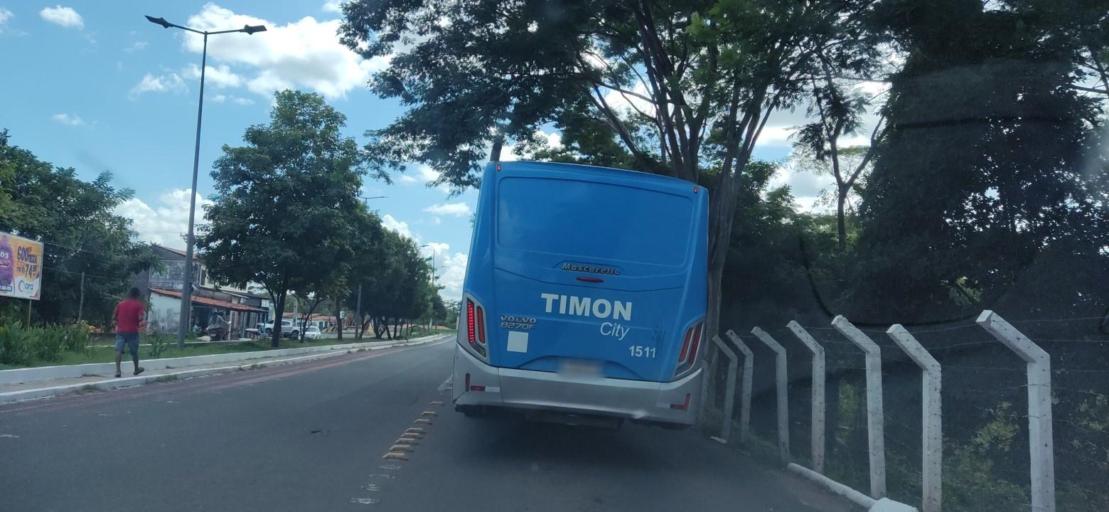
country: BR
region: Maranhao
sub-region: Timon
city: Timon
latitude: -5.0895
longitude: -42.8255
